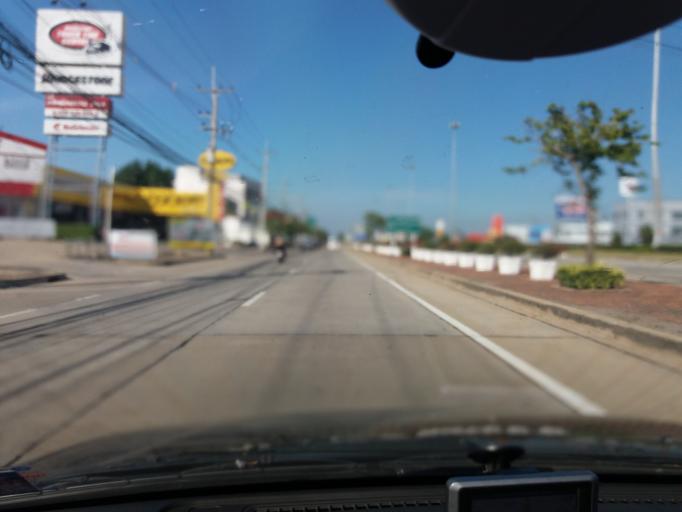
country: TH
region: Suphan Buri
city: Suphan Buri
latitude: 14.4775
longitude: 100.1312
